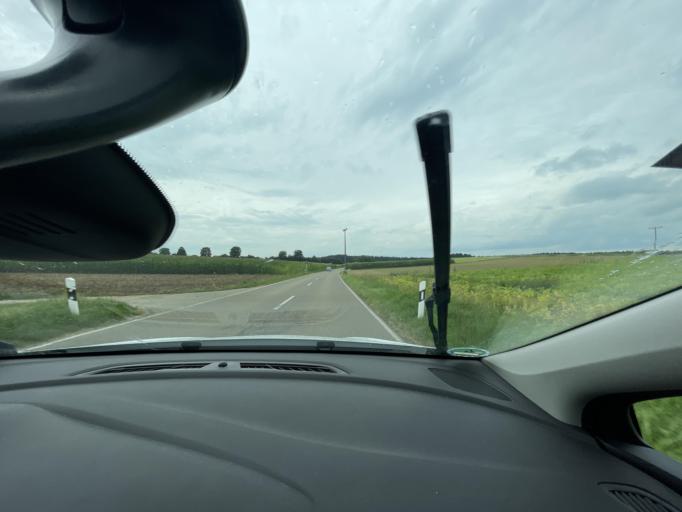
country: DE
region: Bavaria
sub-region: Swabia
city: Aindling
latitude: 48.5585
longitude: 10.9619
